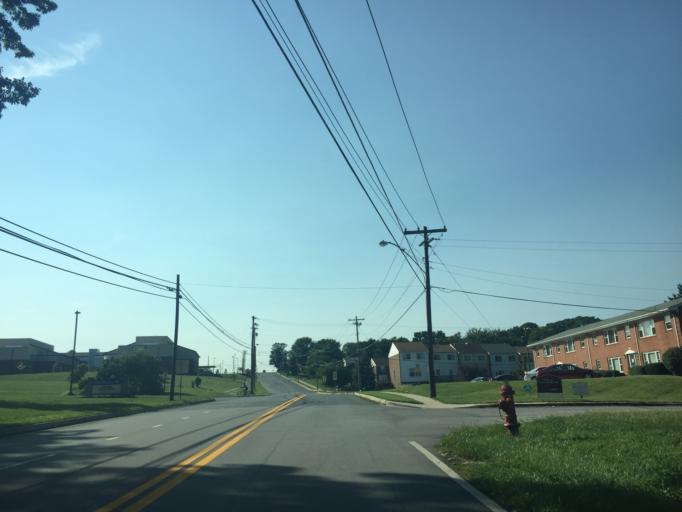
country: US
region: Maryland
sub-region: Carroll County
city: Mount Airy
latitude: 39.3804
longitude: -77.1438
